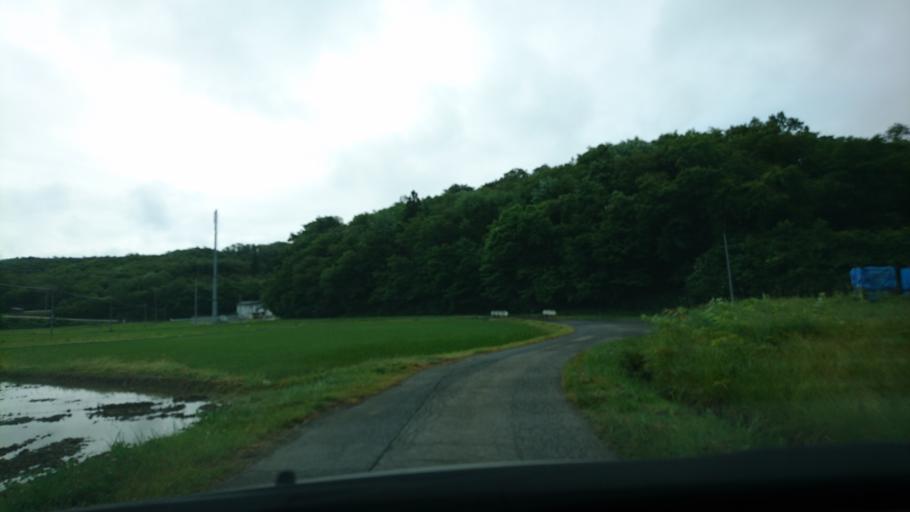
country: JP
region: Iwate
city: Ichinoseki
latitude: 38.8964
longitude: 141.1491
